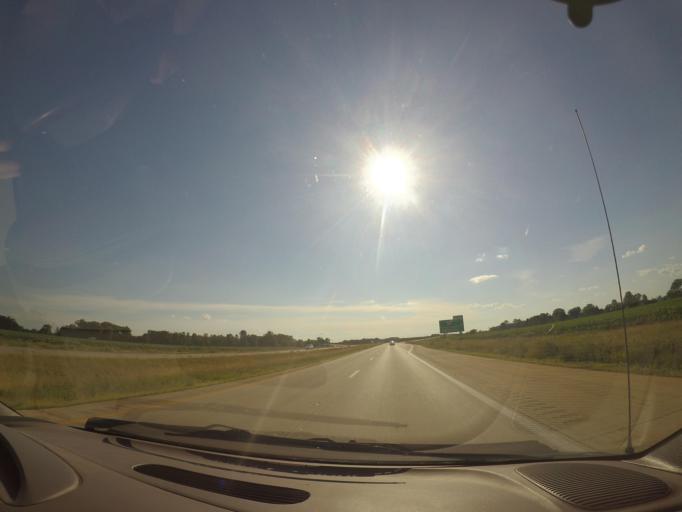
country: US
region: Ohio
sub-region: Lucas County
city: Whitehouse
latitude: 41.4561
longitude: -83.8177
